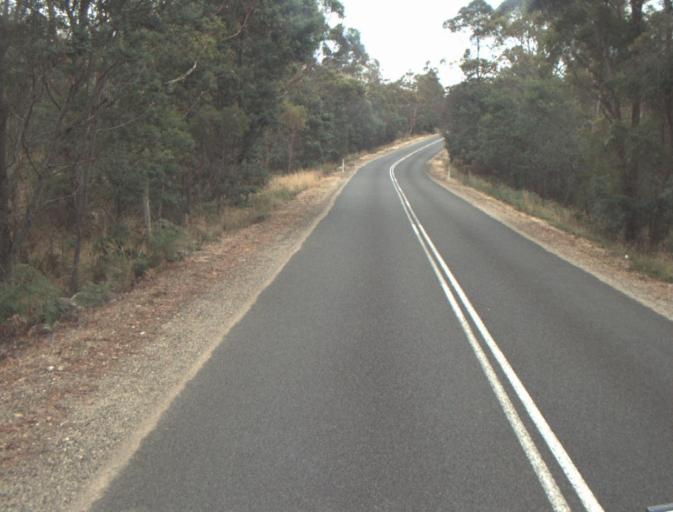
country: AU
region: Tasmania
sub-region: Northern Midlands
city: Evandale
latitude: -41.4981
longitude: 147.3843
